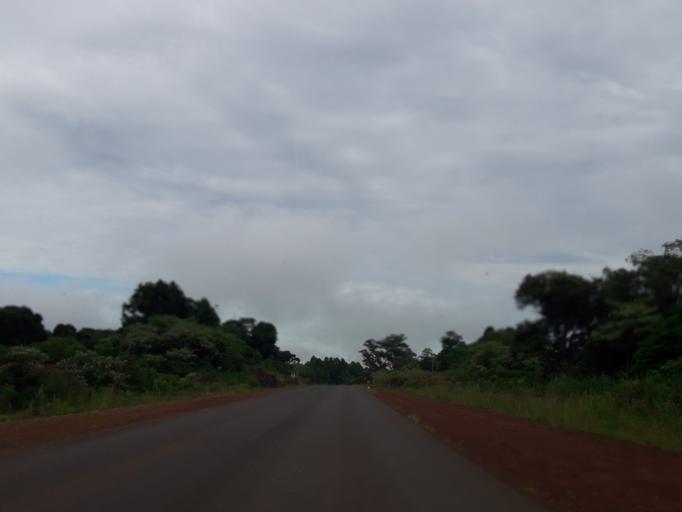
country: AR
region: Misiones
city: Bernardo de Irigoyen
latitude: -26.4262
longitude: -53.8437
